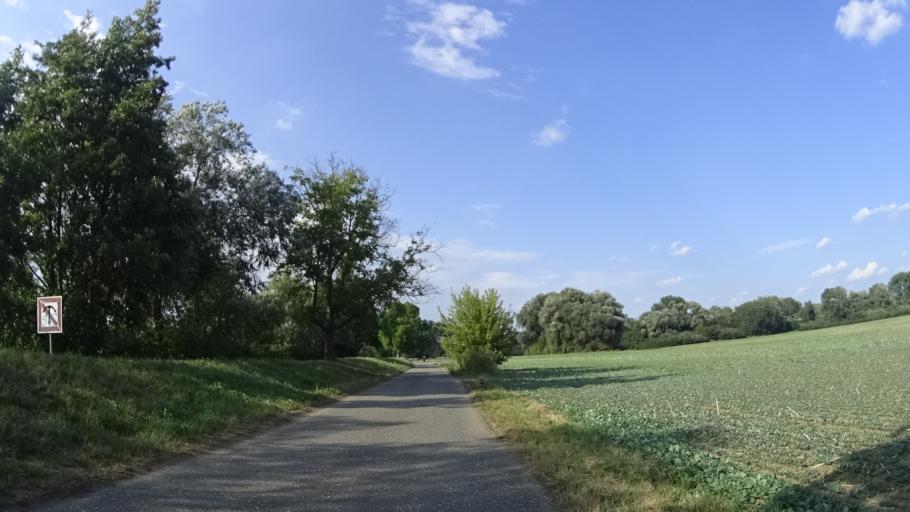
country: CZ
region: Zlin
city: Spytihnev
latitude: 49.1389
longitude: 17.5049
